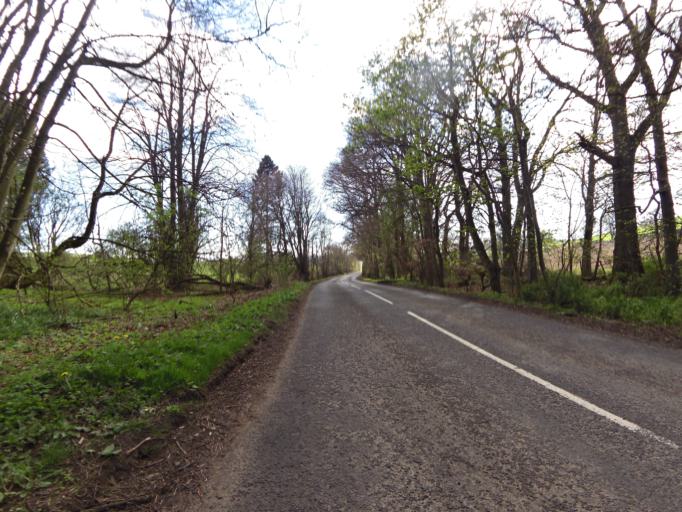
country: GB
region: Scotland
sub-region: Fife
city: Auchtermuchty
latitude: 56.3156
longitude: -3.2332
